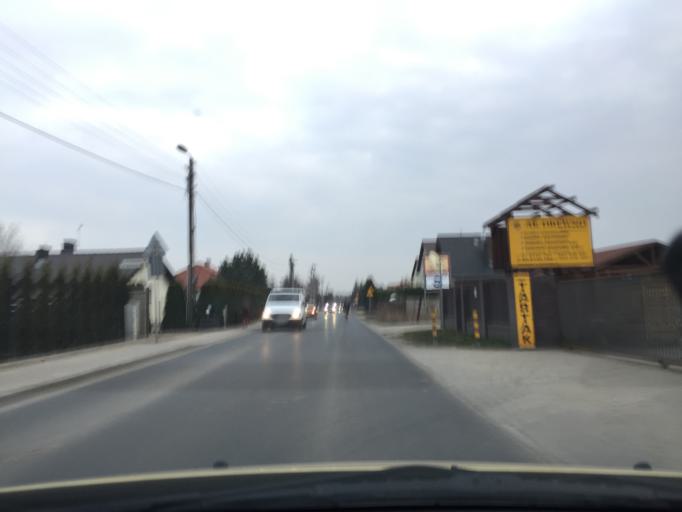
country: PL
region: Greater Poland Voivodeship
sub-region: Powiat poznanski
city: Plewiska
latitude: 52.3882
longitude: 16.7960
